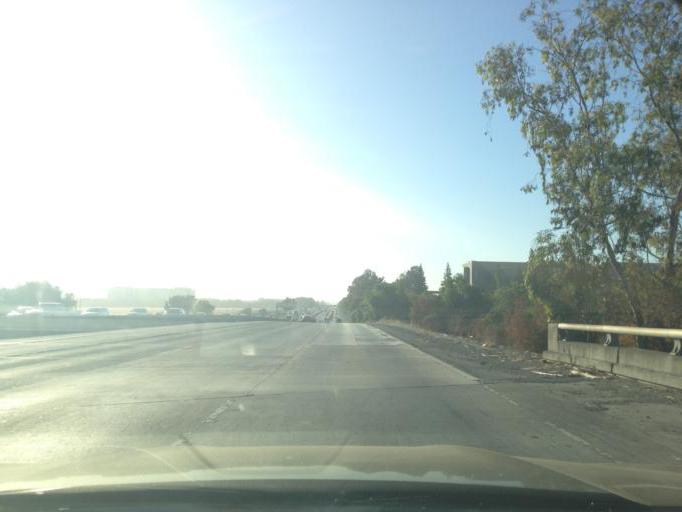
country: US
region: California
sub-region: Santa Clara County
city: Mountain View
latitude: 37.4040
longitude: -122.0512
